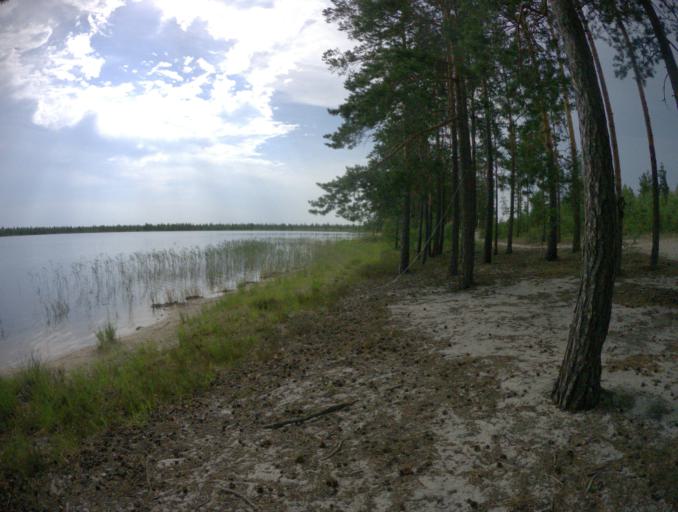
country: RU
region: Ivanovo
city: Talitsy
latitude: 56.4314
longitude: 42.3277
